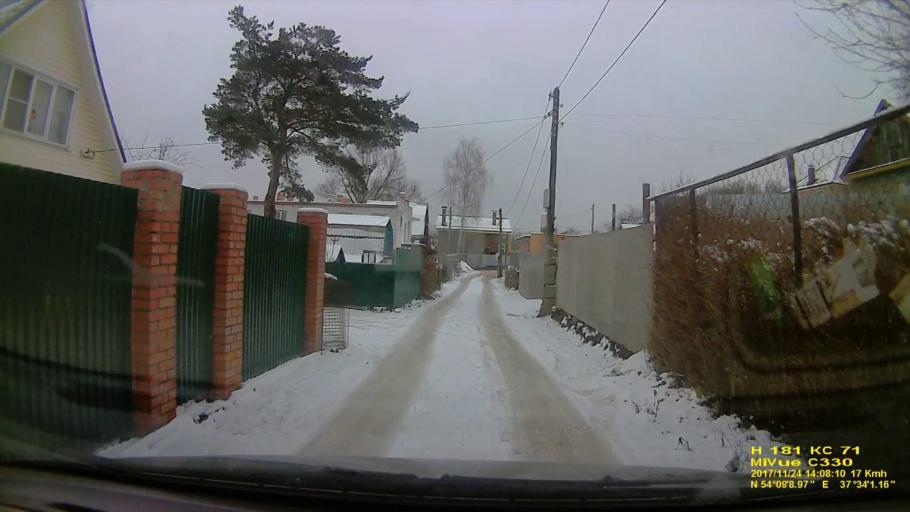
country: RU
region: Tula
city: Mendeleyevskiy
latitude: 54.1530
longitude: 37.5634
